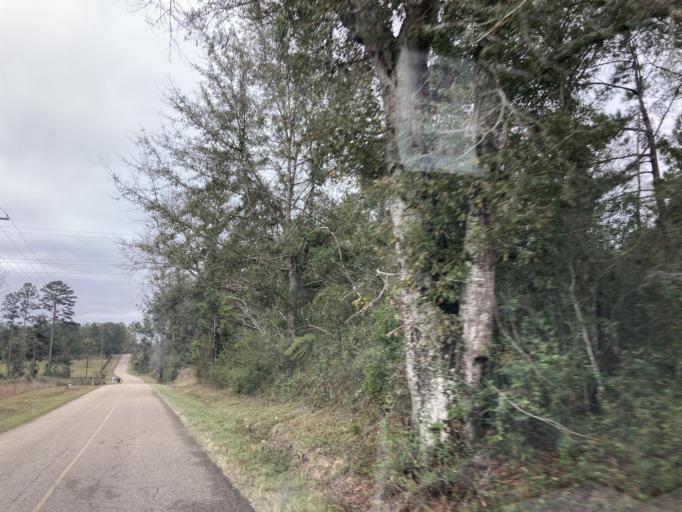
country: US
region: Mississippi
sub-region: Lamar County
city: West Hattiesburg
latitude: 31.2679
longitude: -89.5059
